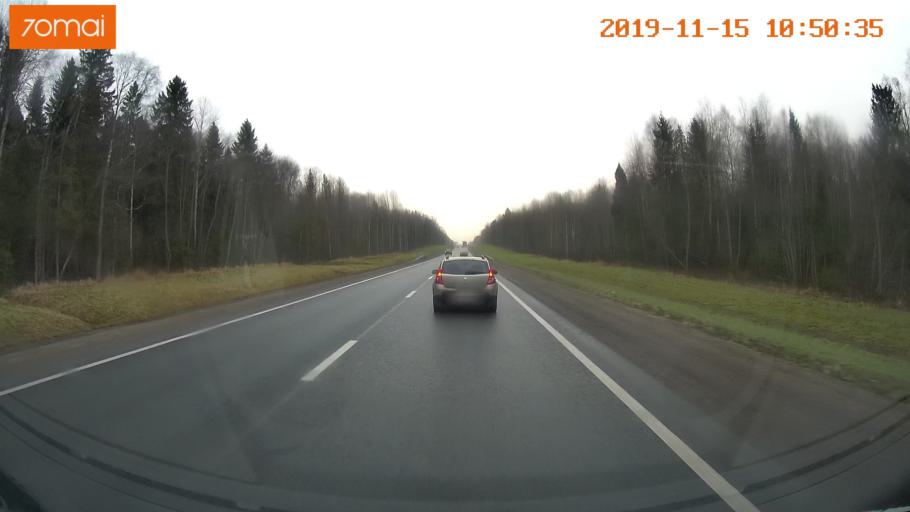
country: RU
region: Vologda
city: Chebsara
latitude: 59.1845
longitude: 38.6852
